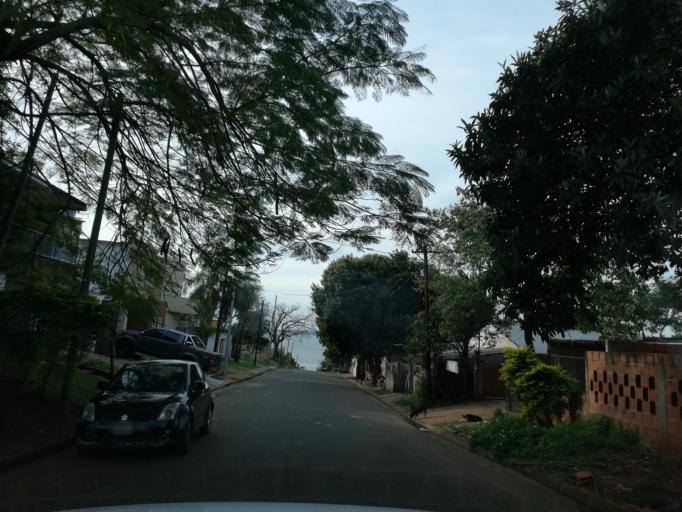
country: AR
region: Misiones
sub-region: Departamento de Capital
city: Posadas
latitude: -27.3568
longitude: -55.9189
